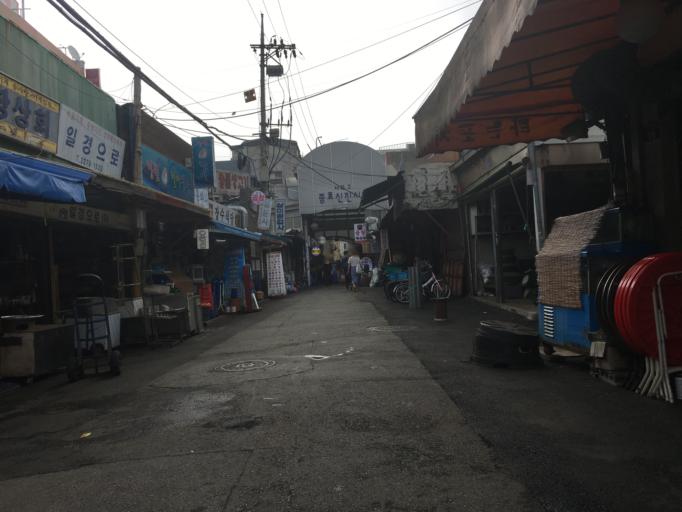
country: KR
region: Seoul
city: Seoul
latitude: 37.5705
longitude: 127.0044
